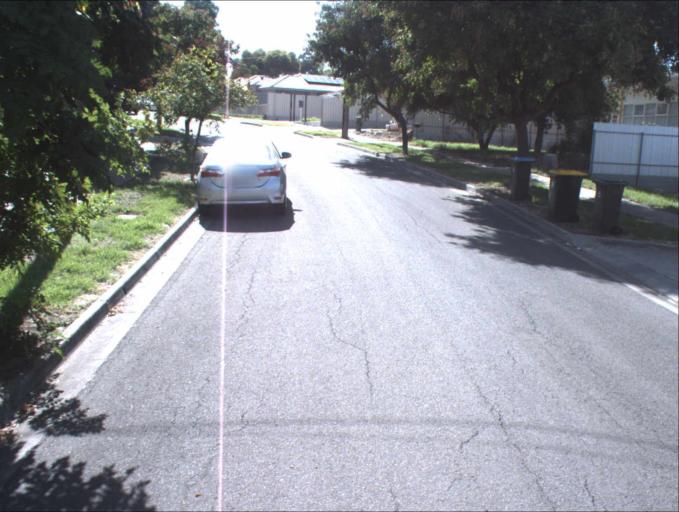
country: AU
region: South Australia
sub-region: Port Adelaide Enfield
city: Gilles Plains
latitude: -34.8635
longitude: 138.6557
